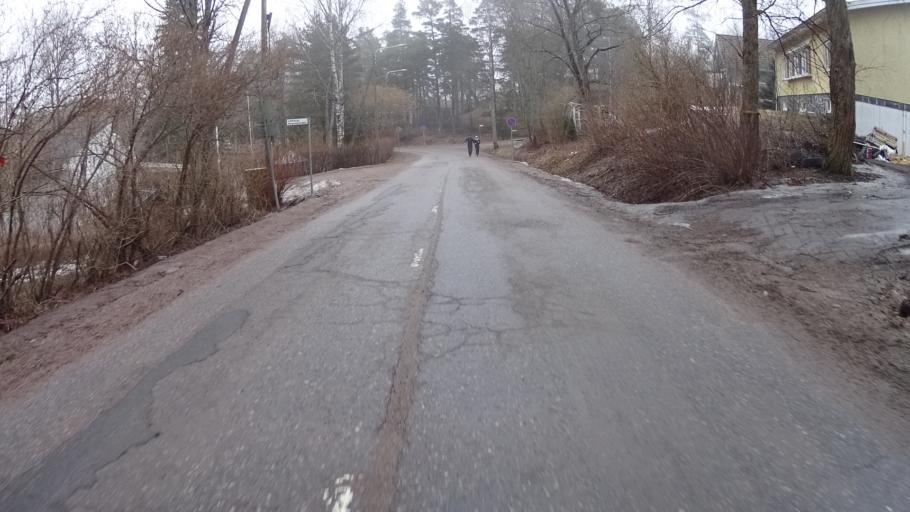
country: FI
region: Uusimaa
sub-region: Helsinki
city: Kilo
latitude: 60.2588
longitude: 24.7775
